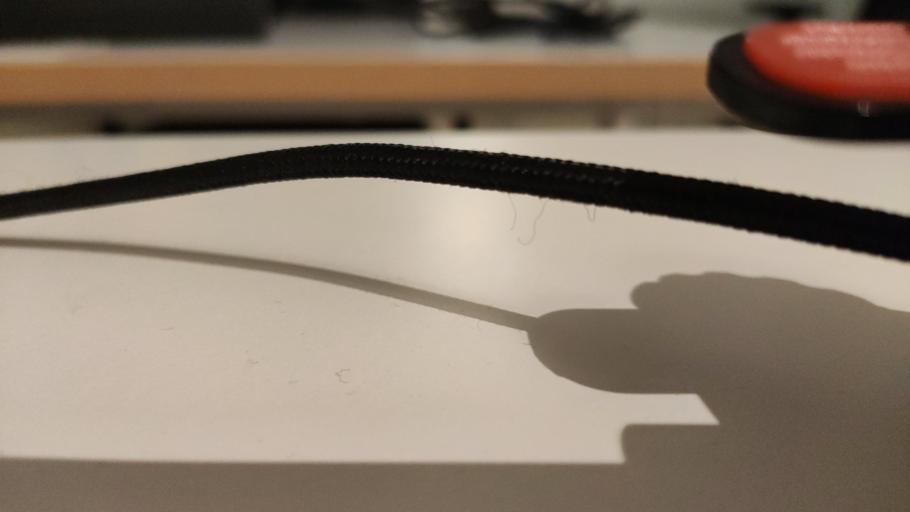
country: RU
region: Moskovskaya
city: Novosin'kovo
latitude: 56.3869
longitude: 37.3167
